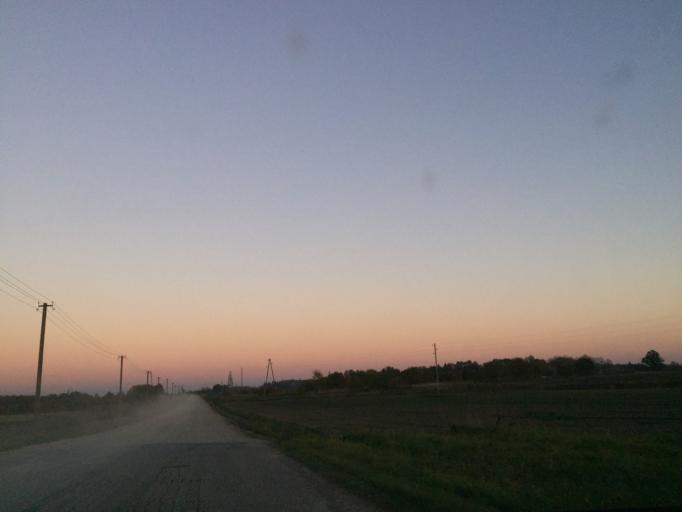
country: LT
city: Akmene
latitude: 56.3795
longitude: 22.6437
